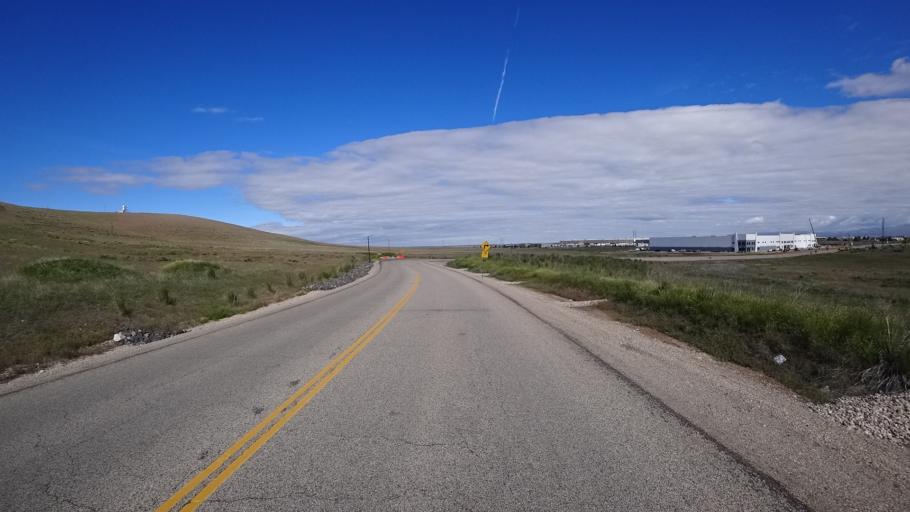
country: US
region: Idaho
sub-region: Ada County
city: Boise
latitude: 43.5121
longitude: -116.1503
